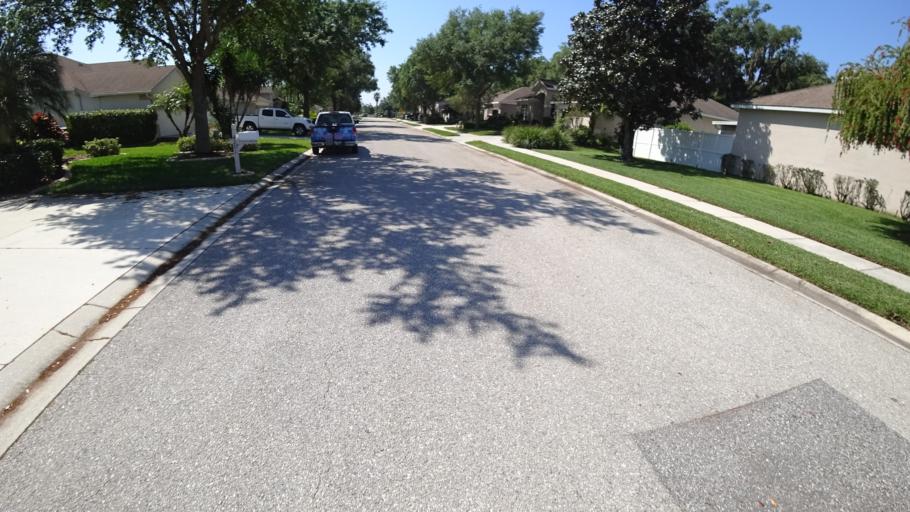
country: US
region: Florida
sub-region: Manatee County
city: Samoset
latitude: 27.4636
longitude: -82.5224
